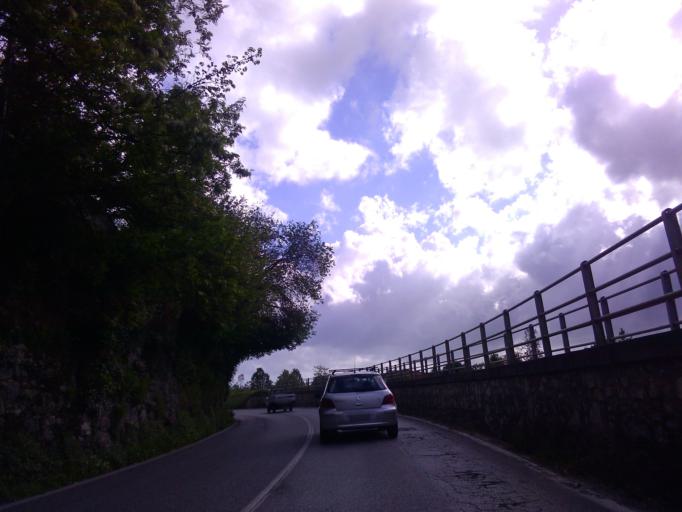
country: IT
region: Tuscany
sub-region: Provincia di Lucca
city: Ripa-Pozzi-Querceta-Ponterosso
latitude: 43.9765
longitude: 10.2204
